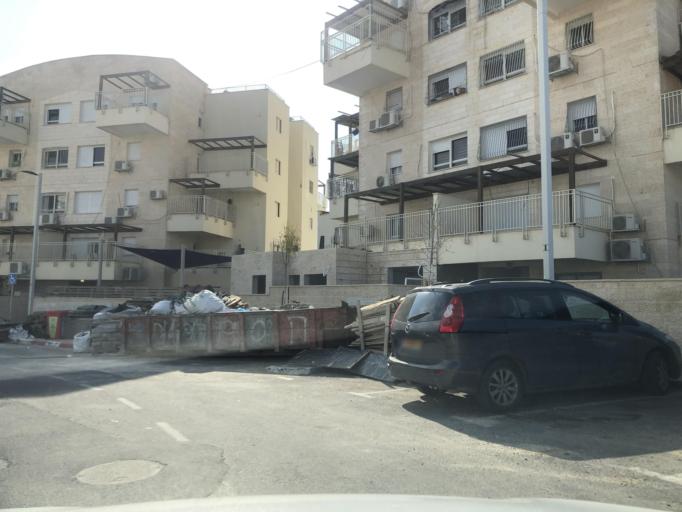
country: IL
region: Jerusalem
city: Modiin Ilit
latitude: 31.9348
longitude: 35.0528
